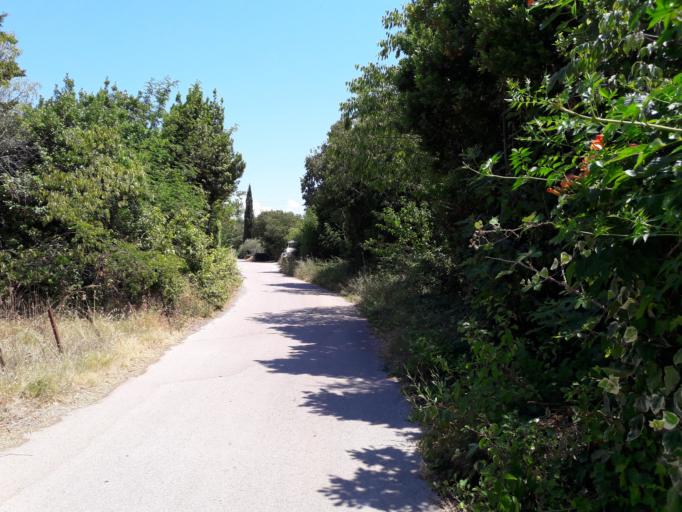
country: HR
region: Sibensko-Kniniska
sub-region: Grad Sibenik
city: Sibenik
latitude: 43.6953
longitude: 15.8371
